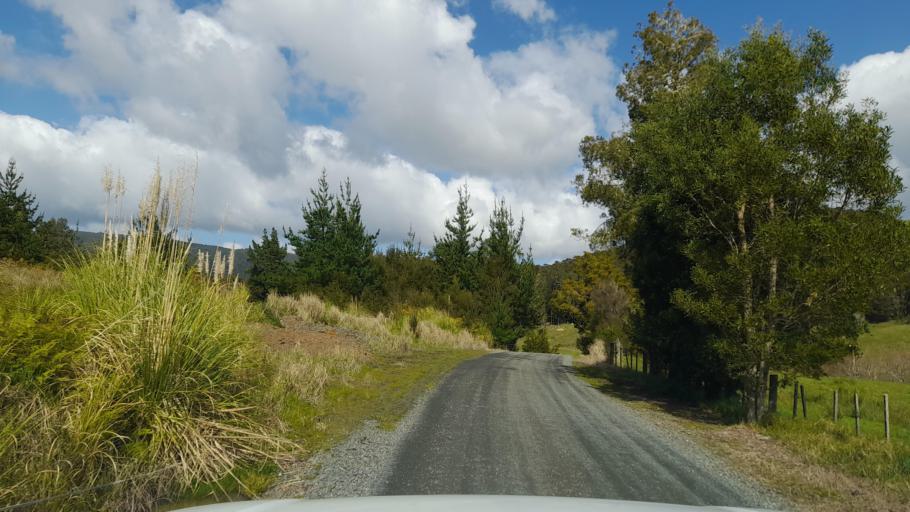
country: NZ
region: Northland
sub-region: Far North District
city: Waimate North
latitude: -35.1465
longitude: 173.7128
